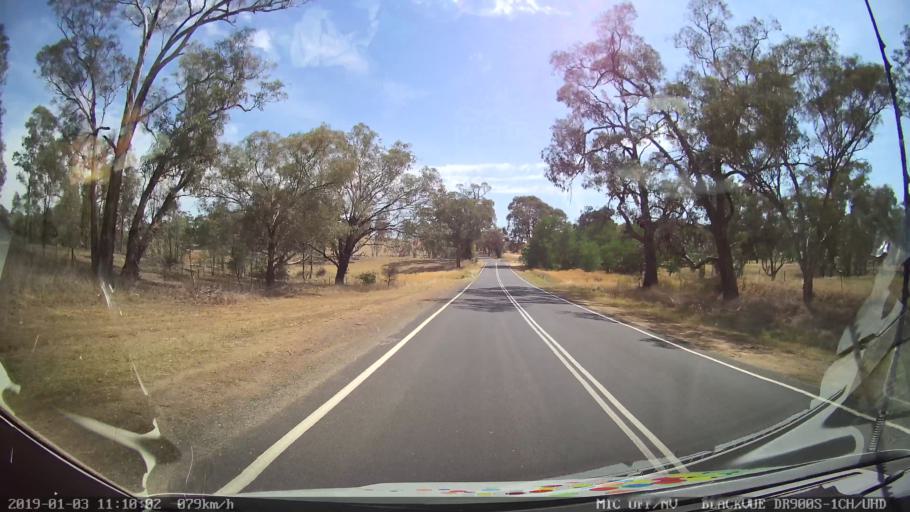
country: AU
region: New South Wales
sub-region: Young
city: Young
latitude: -34.2313
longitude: 148.2569
